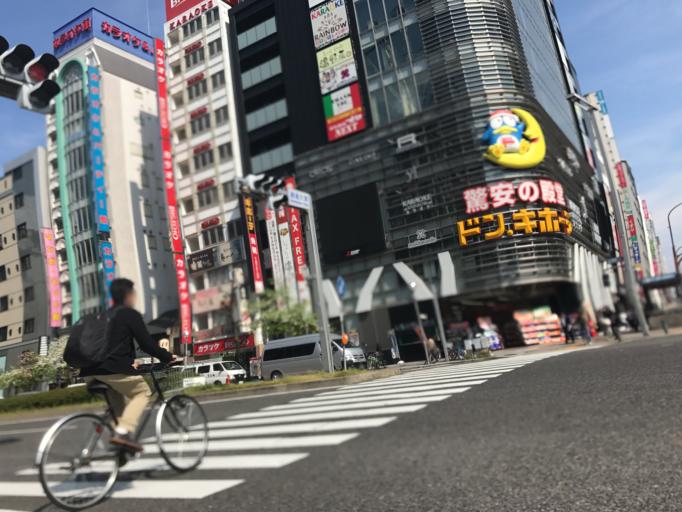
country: JP
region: Aichi
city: Nagoya-shi
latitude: 35.1700
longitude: 136.9068
